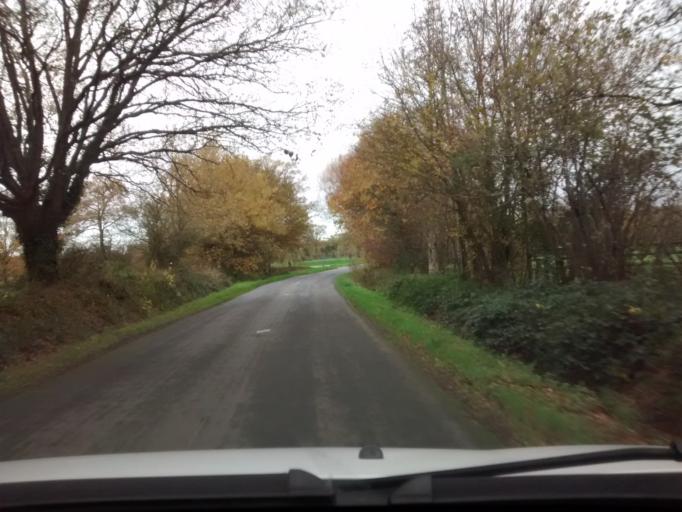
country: FR
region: Brittany
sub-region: Departement d'Ille-et-Vilaine
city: Montreuil-sous-Perouse
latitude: 48.1471
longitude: -1.2631
